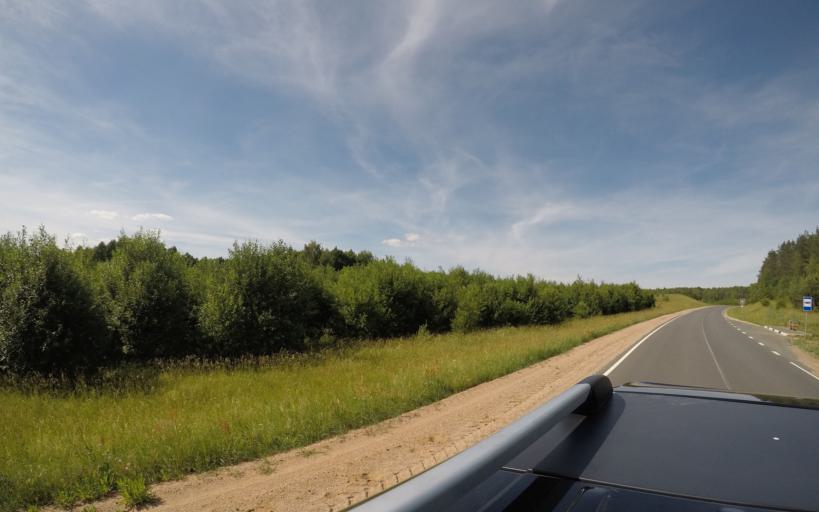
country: BY
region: Grodnenskaya
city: Hal'shany
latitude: 54.2718
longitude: 26.0320
